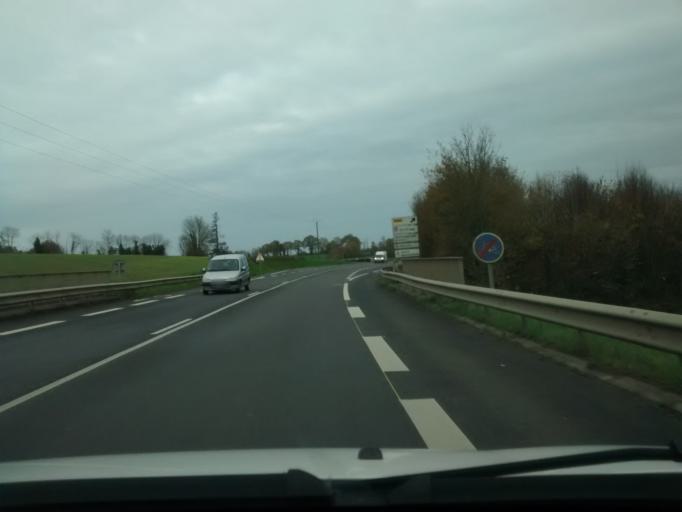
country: FR
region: Brittany
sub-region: Departement d'Ille-et-Vilaine
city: Poce-les-Bois
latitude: 48.1198
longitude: -1.2323
